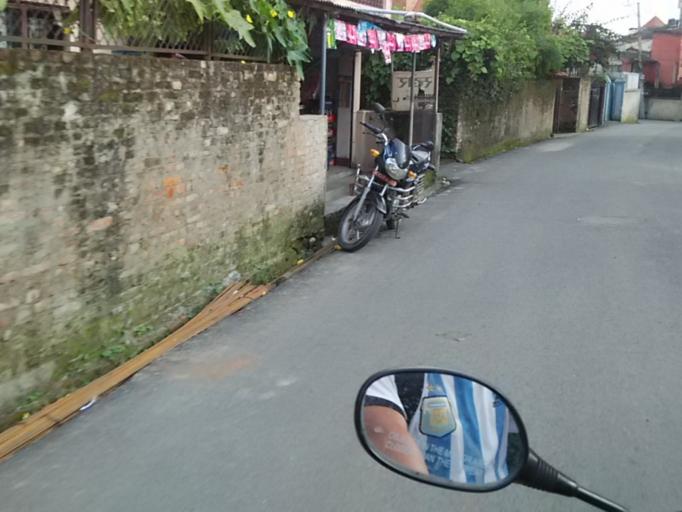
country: NP
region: Central Region
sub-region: Bagmati Zone
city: Kathmandu
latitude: 27.7331
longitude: 85.3363
